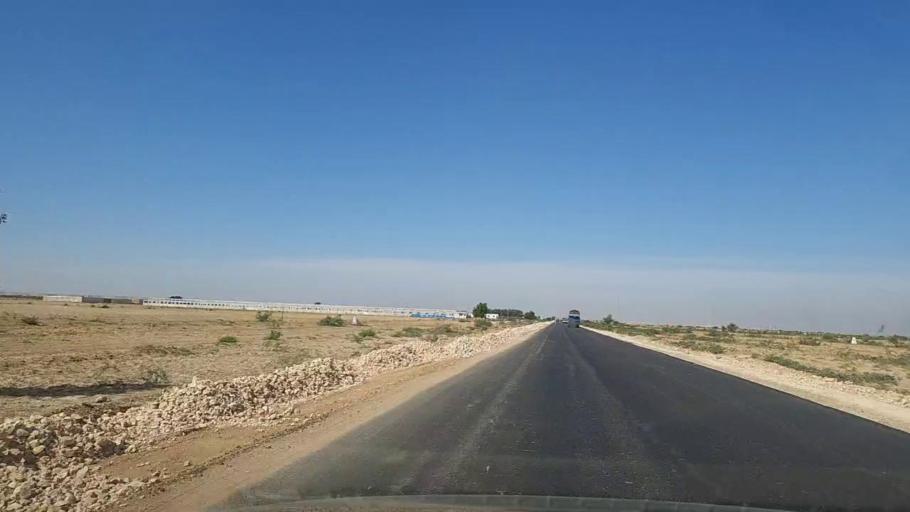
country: PK
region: Sindh
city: Kotri
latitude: 25.2543
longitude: 68.2258
